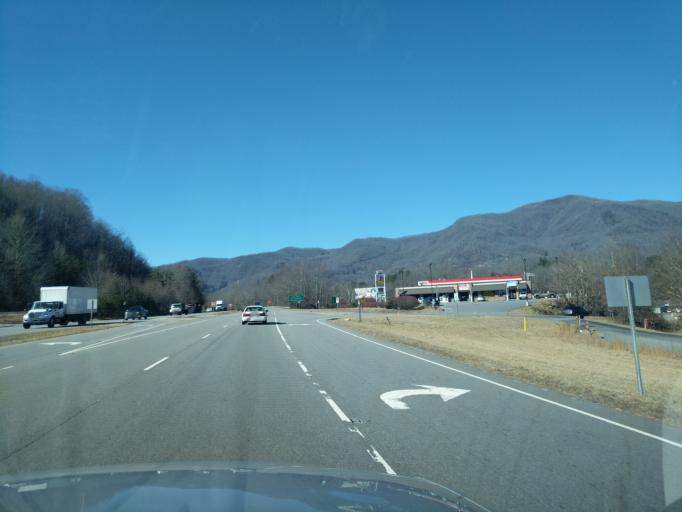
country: US
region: North Carolina
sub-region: Jackson County
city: Sylva
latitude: 35.3916
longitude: -83.1862
